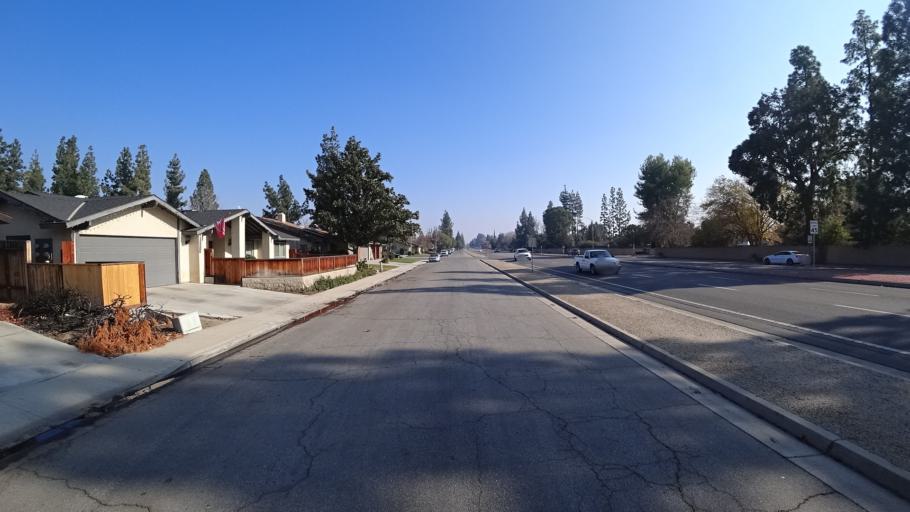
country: US
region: California
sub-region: Kern County
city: Greenacres
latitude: 35.3545
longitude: -119.0873
